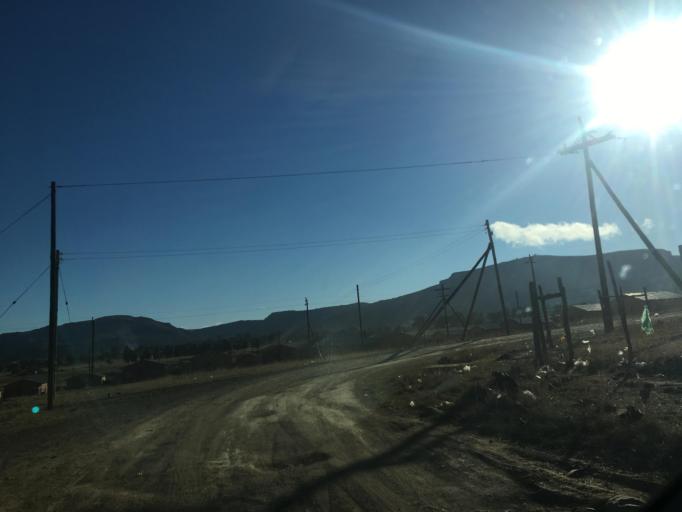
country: ZA
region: Eastern Cape
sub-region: Chris Hani District Municipality
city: Cala
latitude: -31.5394
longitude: 27.6807
